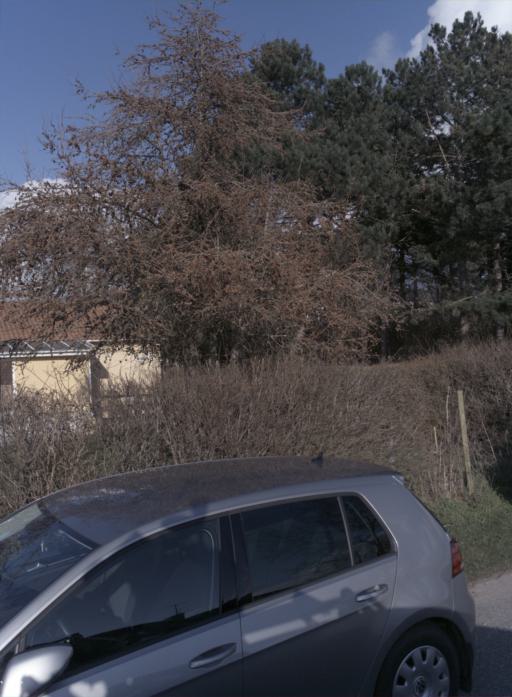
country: DK
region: Zealand
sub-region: Kalundborg Kommune
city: Kalundborg
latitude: 55.6917
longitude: 11.1544
